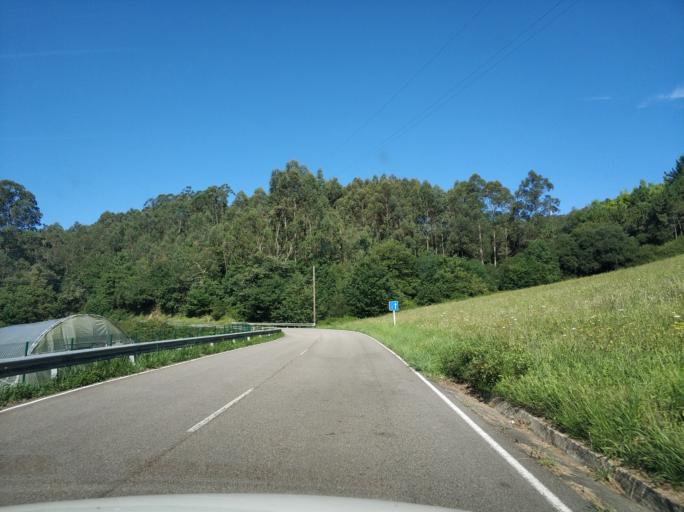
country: ES
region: Asturias
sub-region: Province of Asturias
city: Cudillero
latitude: 43.5649
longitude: -6.2369
